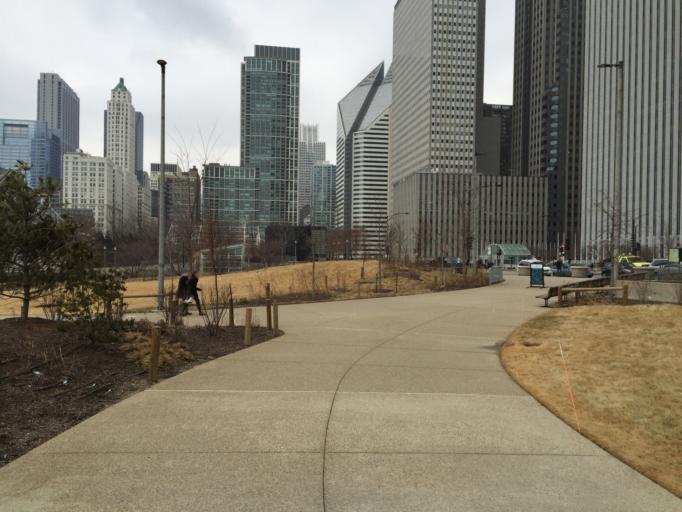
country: US
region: Illinois
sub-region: Cook County
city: Chicago
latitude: 41.8840
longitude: -87.6196
